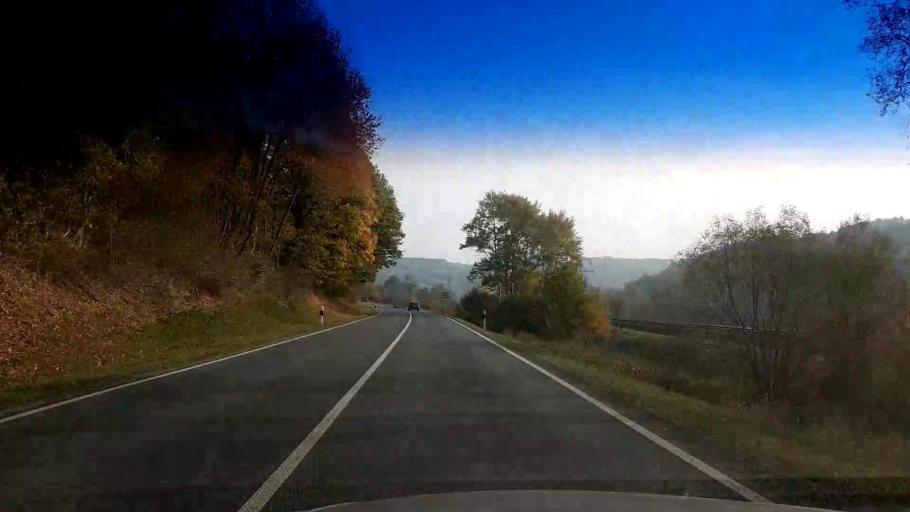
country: DE
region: Bavaria
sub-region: Upper Franconia
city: Untersteinach
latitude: 50.1115
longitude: 11.4925
